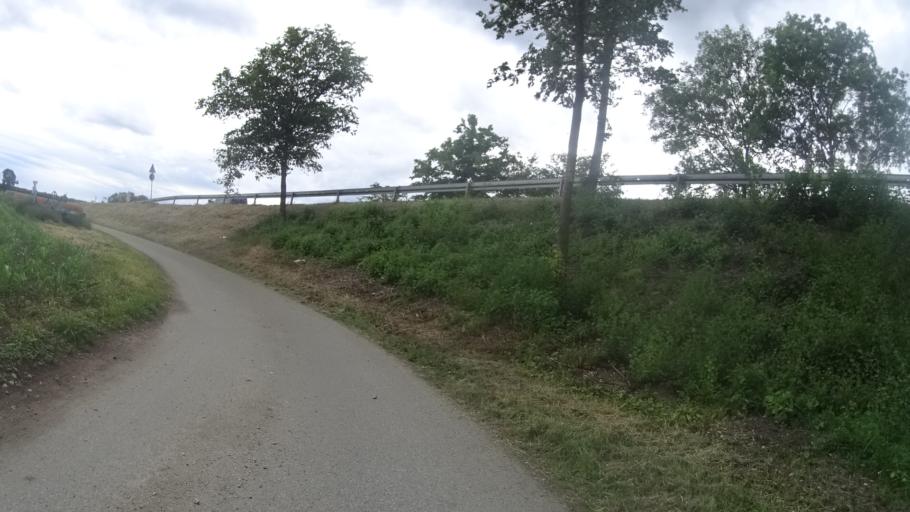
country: DE
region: Bavaria
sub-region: Upper Bavaria
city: Bergkirchen
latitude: 48.2390
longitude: 11.3736
